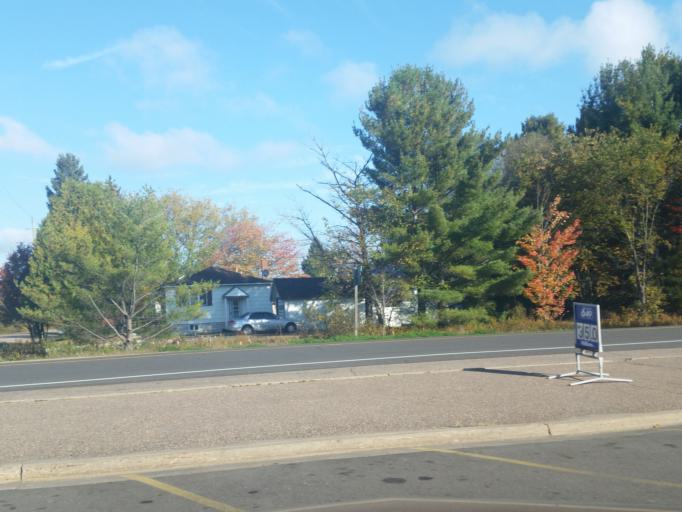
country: CA
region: Ontario
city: Pembroke
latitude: 45.7977
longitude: -77.1707
